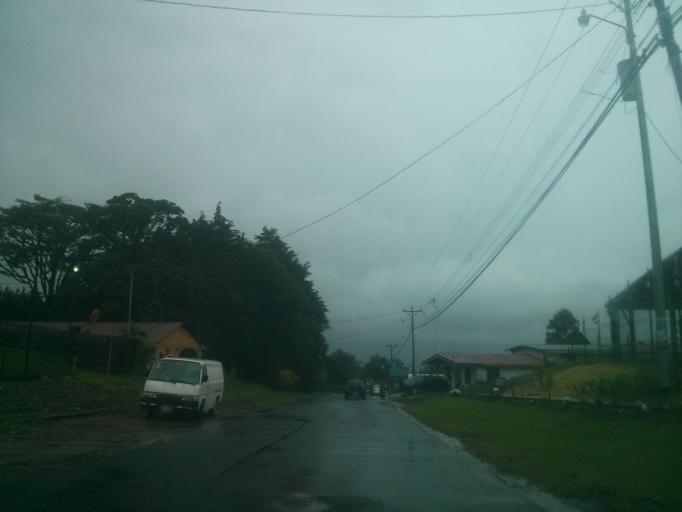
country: CR
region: Alajuela
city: Sabanilla
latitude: 10.1450
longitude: -84.1947
